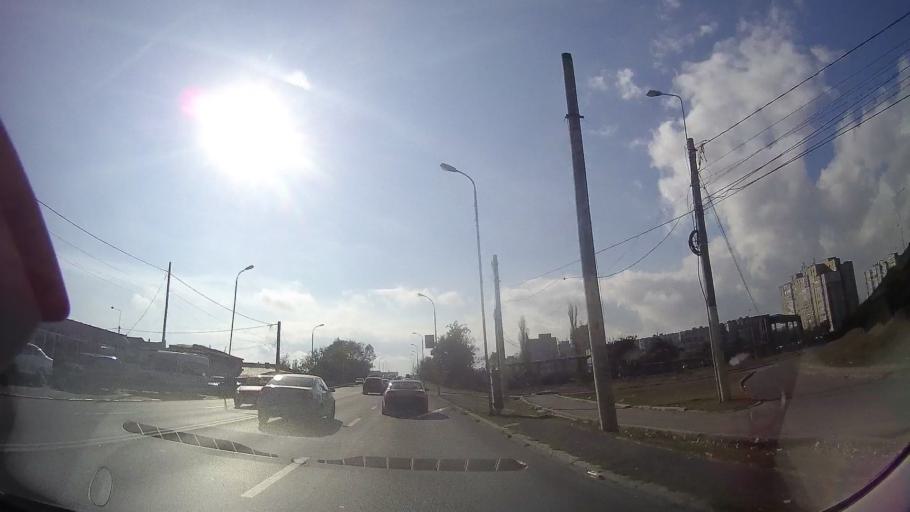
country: RO
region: Constanta
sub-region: Municipiul Constanta
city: Constanta
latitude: 44.1510
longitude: 28.6271
